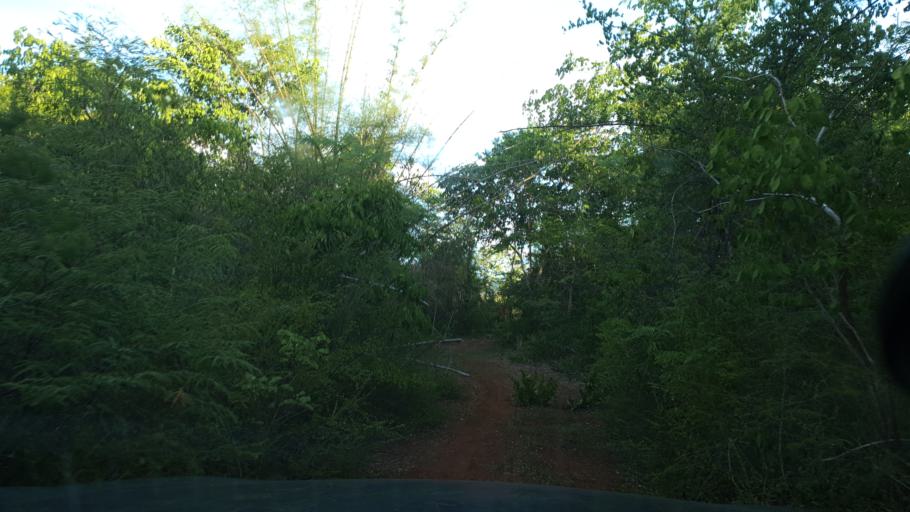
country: TH
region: Lampang
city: Sop Prap
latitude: 17.9638
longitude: 99.3519
